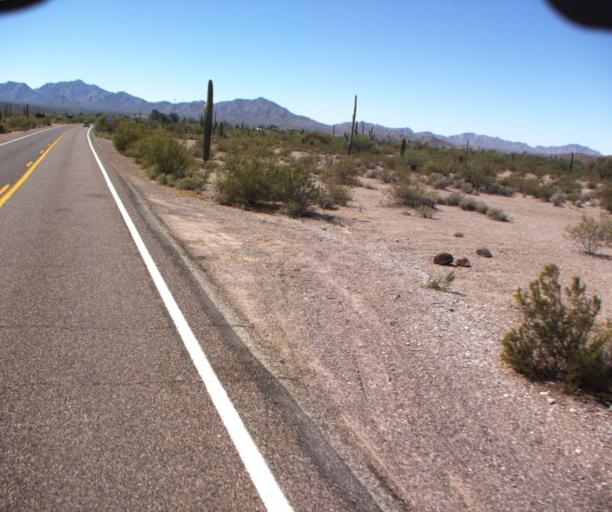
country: MX
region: Sonora
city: Sonoyta
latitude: 31.8915
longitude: -112.8123
